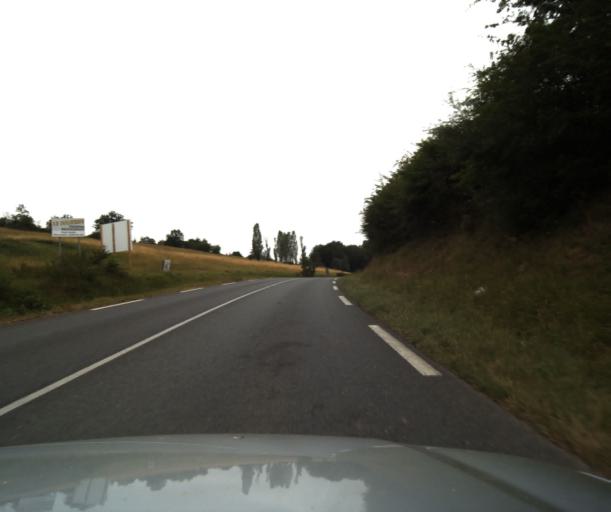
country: FR
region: Midi-Pyrenees
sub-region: Departement du Gers
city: Auch
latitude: 43.6517
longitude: 0.6173
